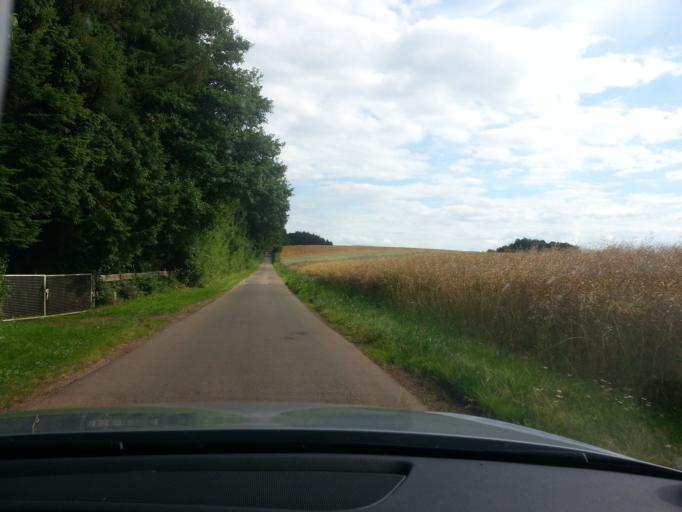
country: DE
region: Saarland
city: Marpingen
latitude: 49.4478
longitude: 7.0922
